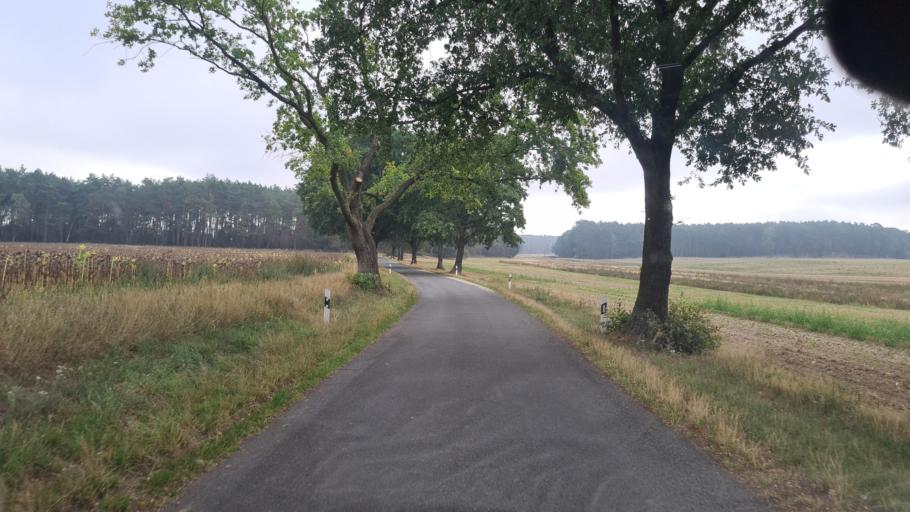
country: DE
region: Brandenburg
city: Niemegk
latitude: 52.0748
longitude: 12.6252
